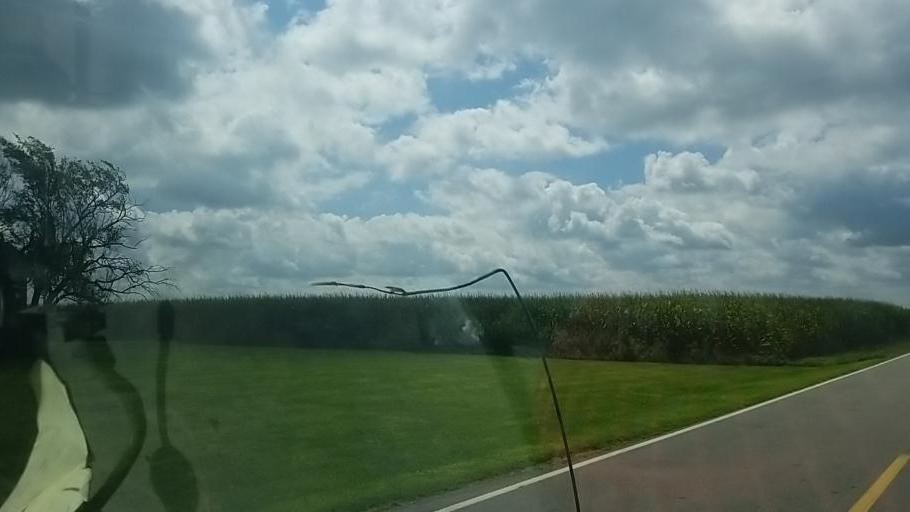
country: US
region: Ohio
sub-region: Fayette County
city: Jeffersonville
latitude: 39.6784
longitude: -83.5042
